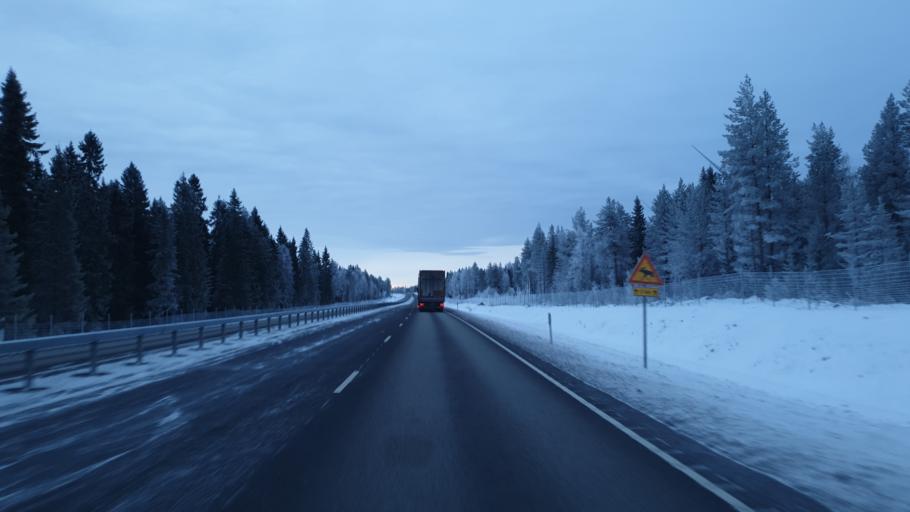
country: FI
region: Lapland
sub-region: Kemi-Tornio
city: Simo
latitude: 65.6378
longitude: 25.1118
